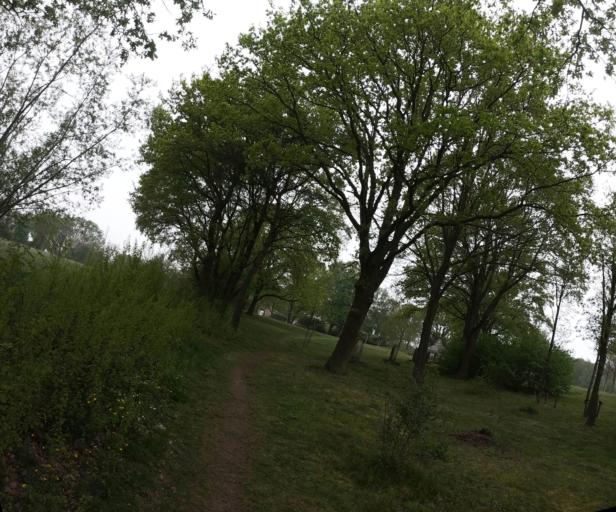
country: BE
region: Flanders
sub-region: Provincie Vlaams-Brabant
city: Gooik
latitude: 50.7744
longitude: 4.1055
